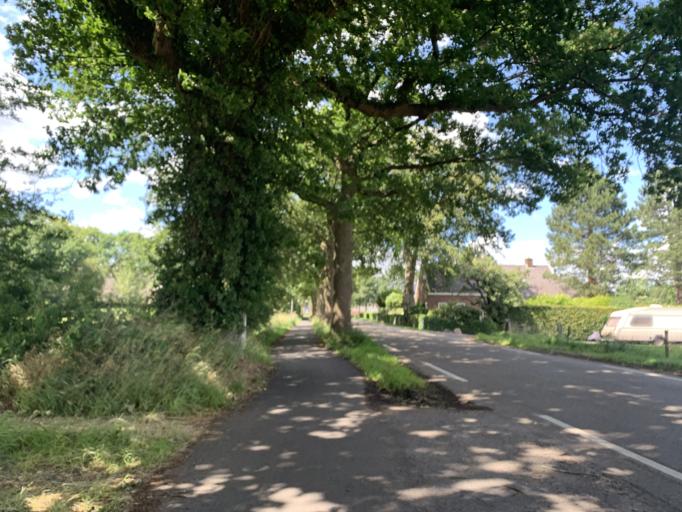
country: NL
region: Groningen
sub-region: Gemeente Haren
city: Haren
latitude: 53.1529
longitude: 6.6443
